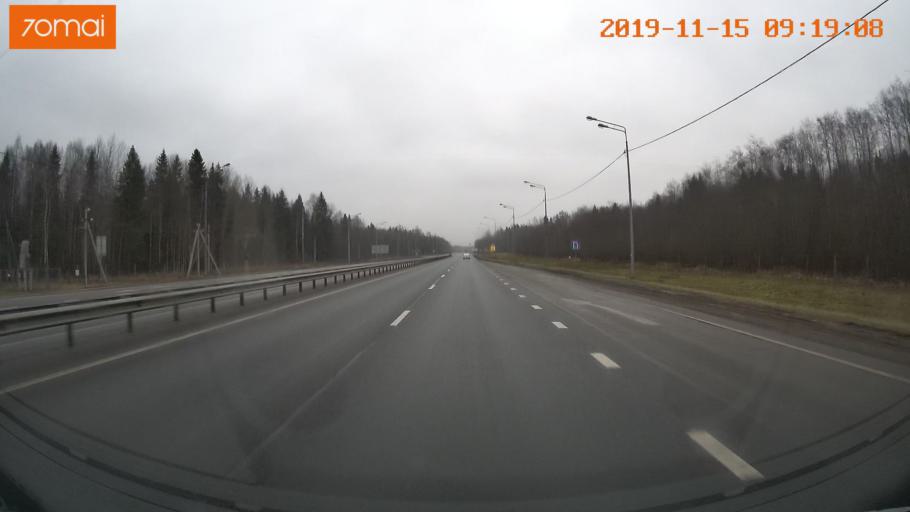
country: RU
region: Vologda
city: Tonshalovo
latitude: 59.2811
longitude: 38.0102
